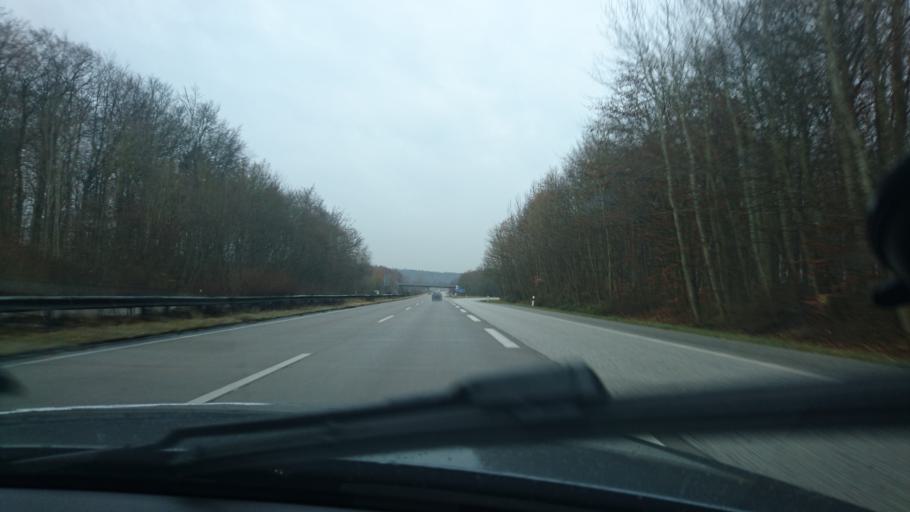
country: DE
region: Schleswig-Holstein
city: Scharbeutz
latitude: 54.0306
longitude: 10.7305
